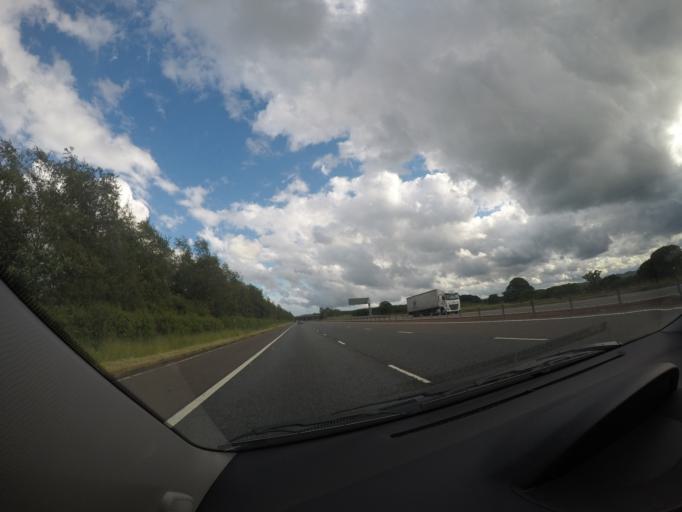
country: GB
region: Scotland
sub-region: Dumfries and Galloway
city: Lochmaben
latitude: 55.1863
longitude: -3.4067
